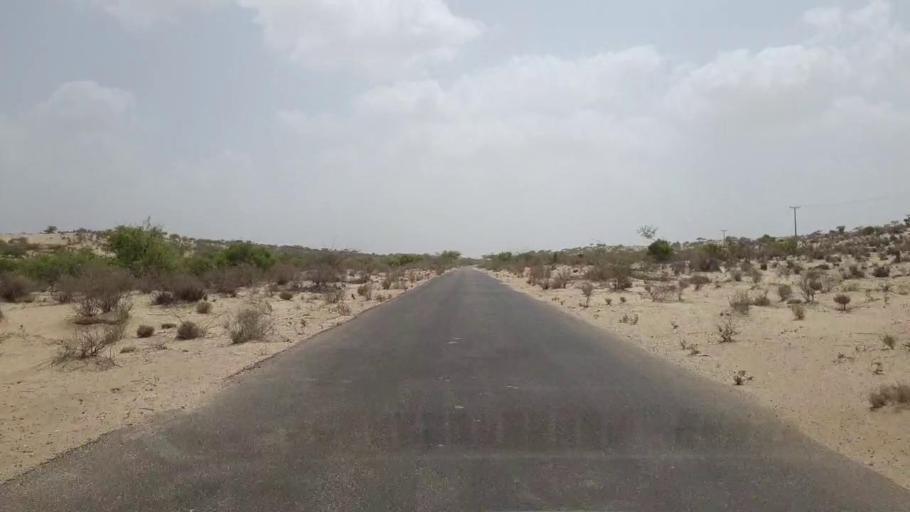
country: PK
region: Sindh
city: Diplo
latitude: 24.3966
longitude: 69.4628
